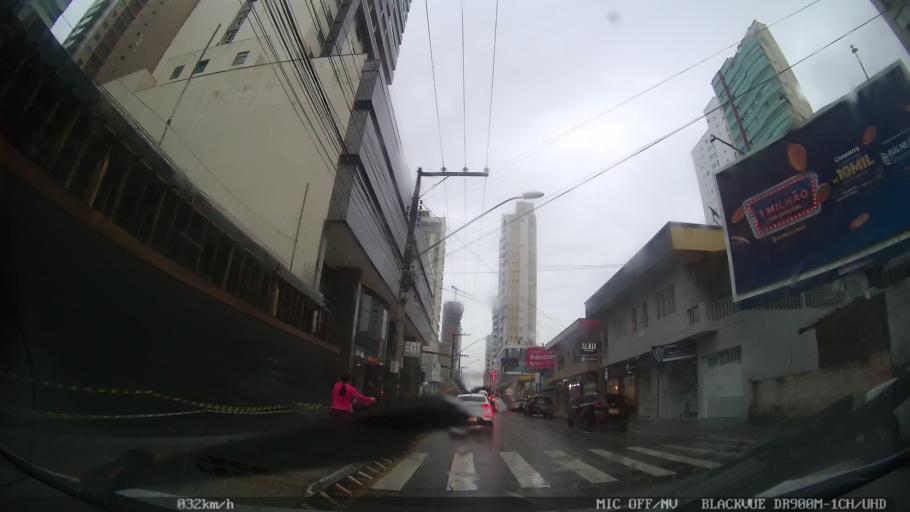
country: BR
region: Santa Catarina
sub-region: Balneario Camboriu
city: Balneario Camboriu
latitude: -26.9875
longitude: -48.6365
